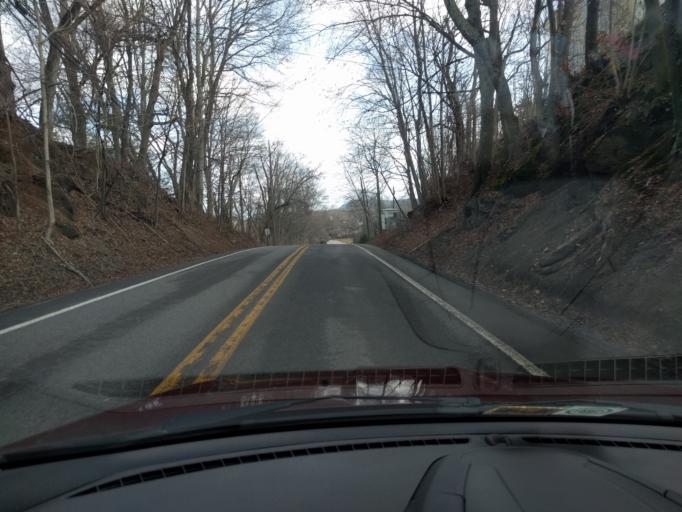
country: US
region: West Virginia
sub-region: Greenbrier County
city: Lewisburg
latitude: 37.7960
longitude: -80.4348
